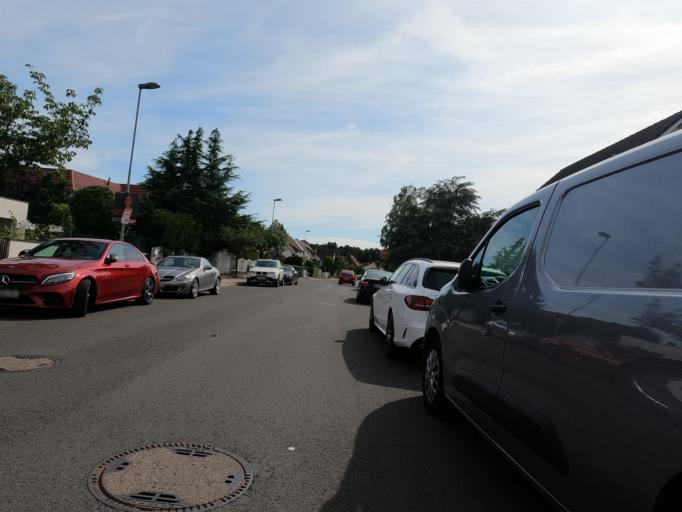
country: DE
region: Hesse
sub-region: Regierungsbezirk Darmstadt
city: Neu Isenburg
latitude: 50.0445
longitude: 8.7008
